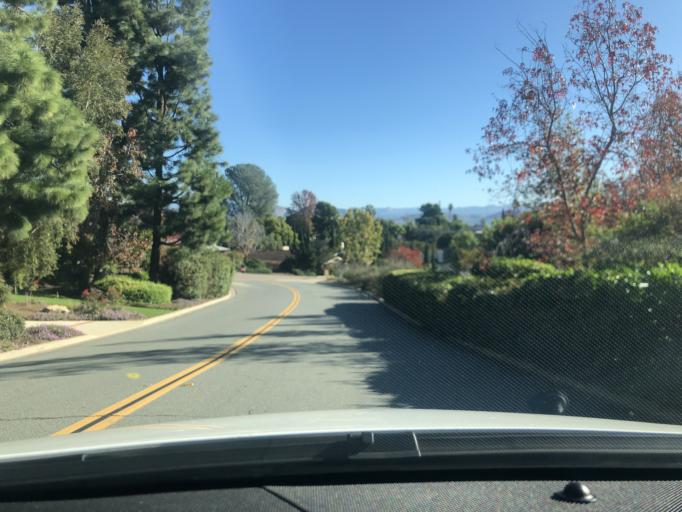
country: US
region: California
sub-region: San Diego County
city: Casa de Oro-Mount Helix
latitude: 32.7691
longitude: -116.9498
